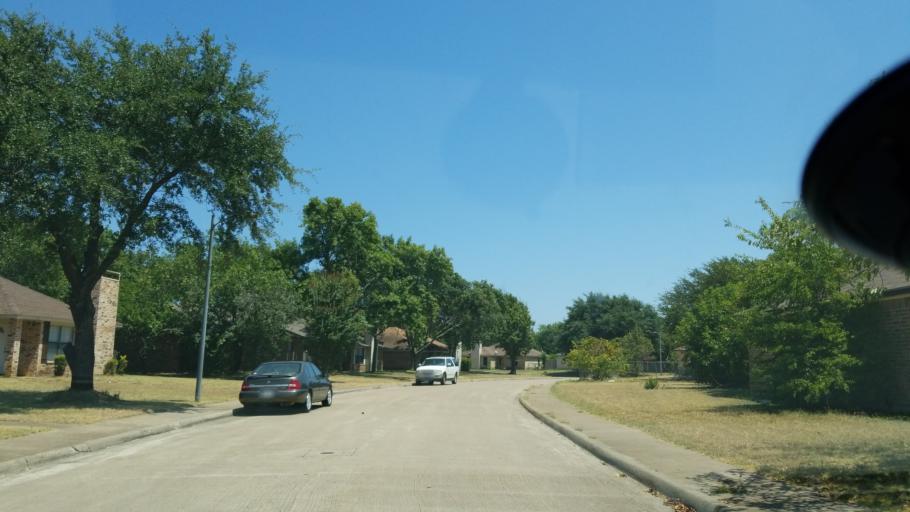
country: US
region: Texas
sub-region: Dallas County
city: Duncanville
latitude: 32.6348
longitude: -96.8852
